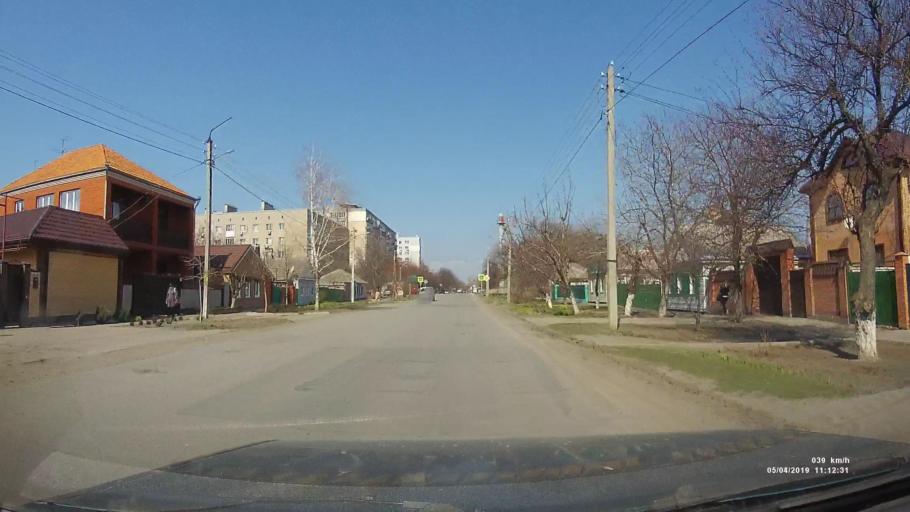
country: RU
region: Rostov
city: Azov
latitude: 47.0983
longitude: 39.4369
